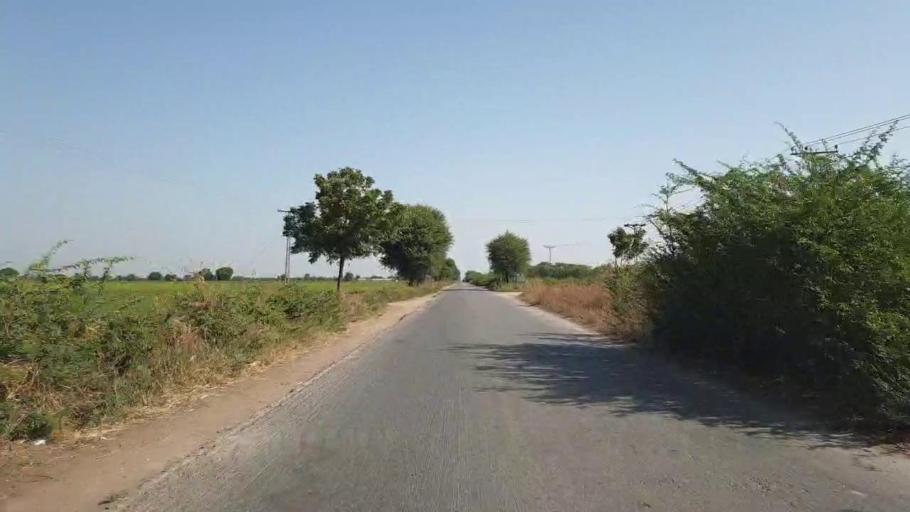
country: PK
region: Sindh
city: Chor
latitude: 25.4421
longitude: 69.7505
